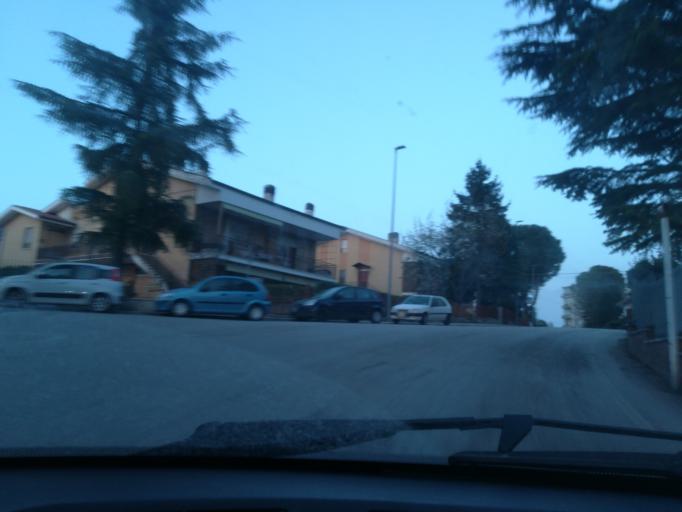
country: IT
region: The Marches
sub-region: Provincia di Macerata
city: Macerata
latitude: 43.2896
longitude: 13.4537
